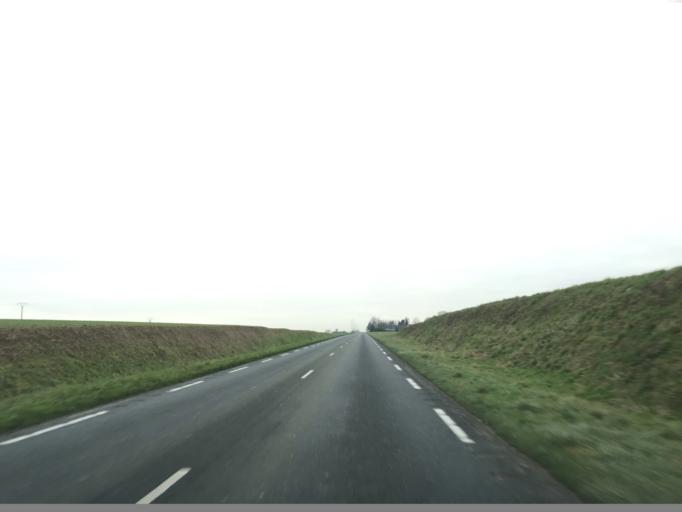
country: FR
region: Haute-Normandie
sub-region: Departement de la Seine-Maritime
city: Montmain
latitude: 49.3867
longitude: 1.2323
